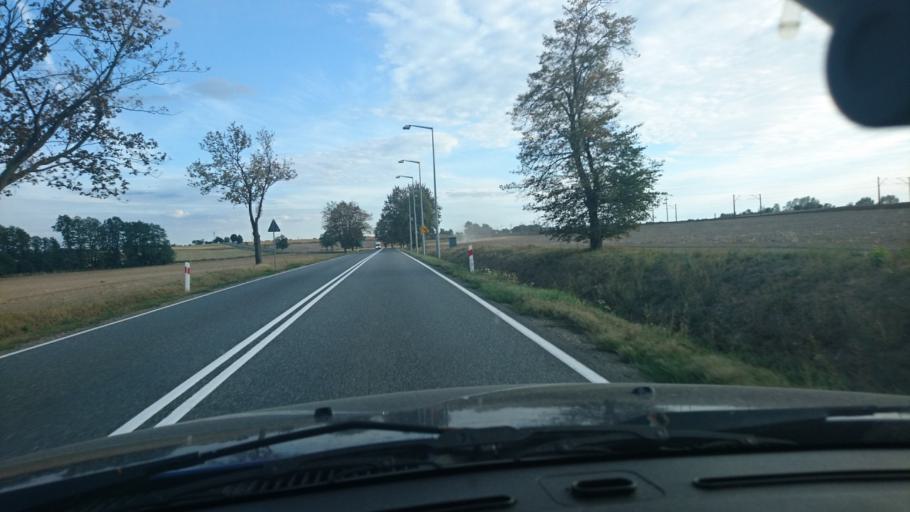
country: PL
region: Opole Voivodeship
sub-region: Powiat kluczborski
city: Byczyna
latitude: 51.1335
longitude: 18.1995
